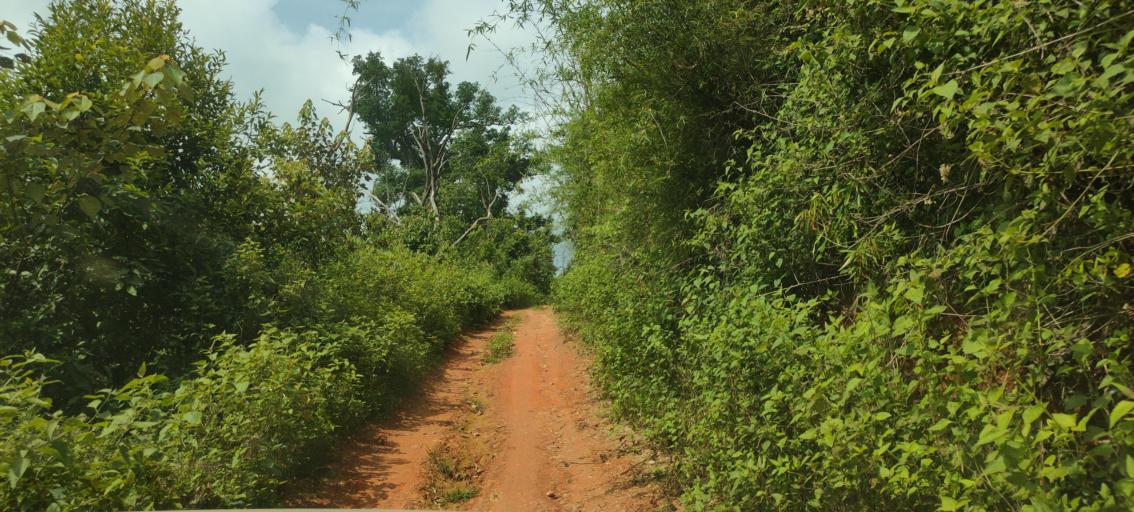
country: LA
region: Loungnamtha
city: Muang Nale
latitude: 20.4261
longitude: 101.4682
